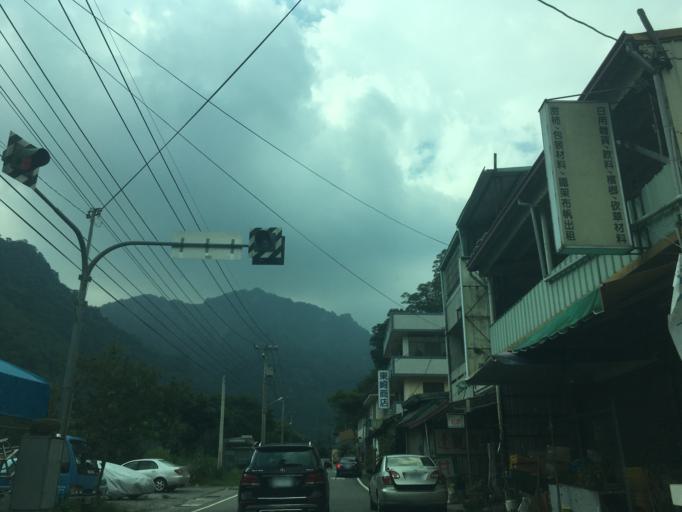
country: TW
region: Taiwan
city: Fengyuan
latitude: 24.3274
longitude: 120.9202
